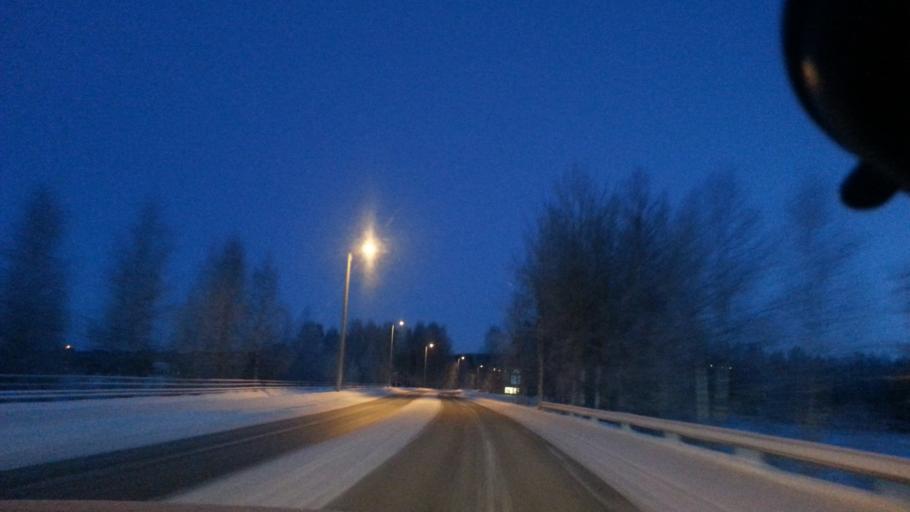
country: FI
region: Lapland
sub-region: Rovaniemi
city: Rovaniemi
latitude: 66.4849
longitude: 25.7499
